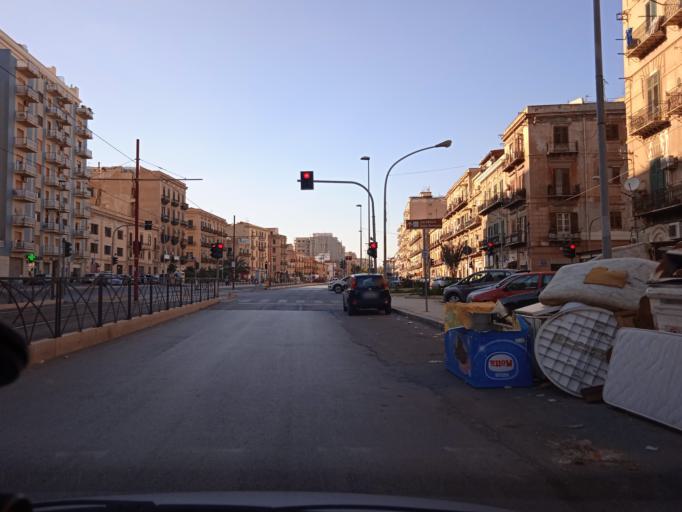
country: IT
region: Sicily
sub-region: Palermo
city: Palermo
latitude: 38.1078
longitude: 13.3718
